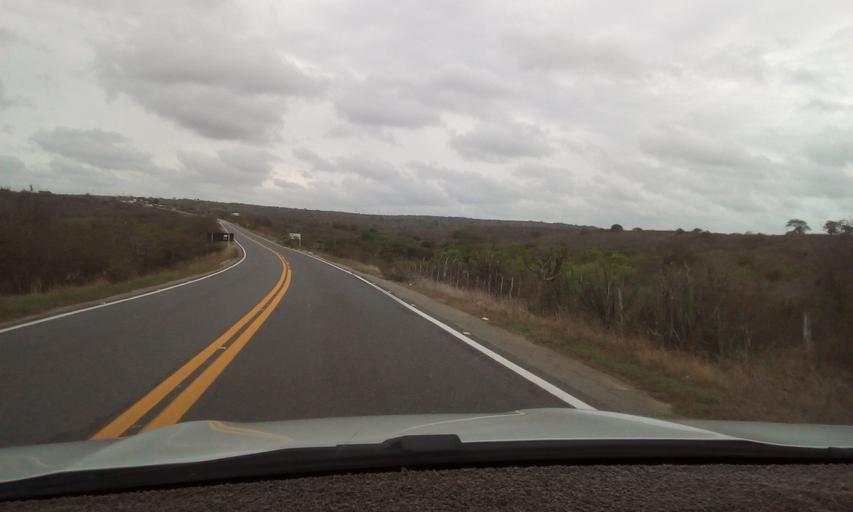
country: BR
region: Paraiba
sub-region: Areia
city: Remigio
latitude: -6.9474
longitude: -35.8188
